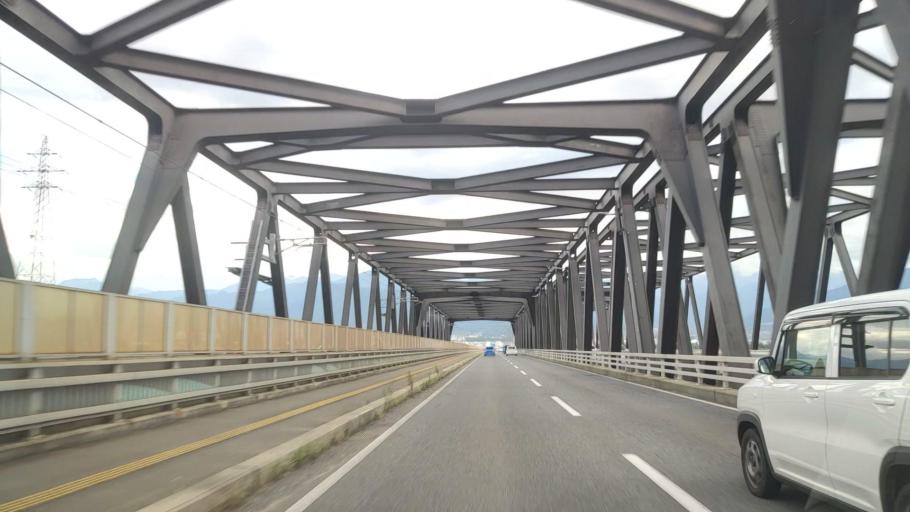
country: JP
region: Nagano
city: Suzaka
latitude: 36.6625
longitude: 138.2707
